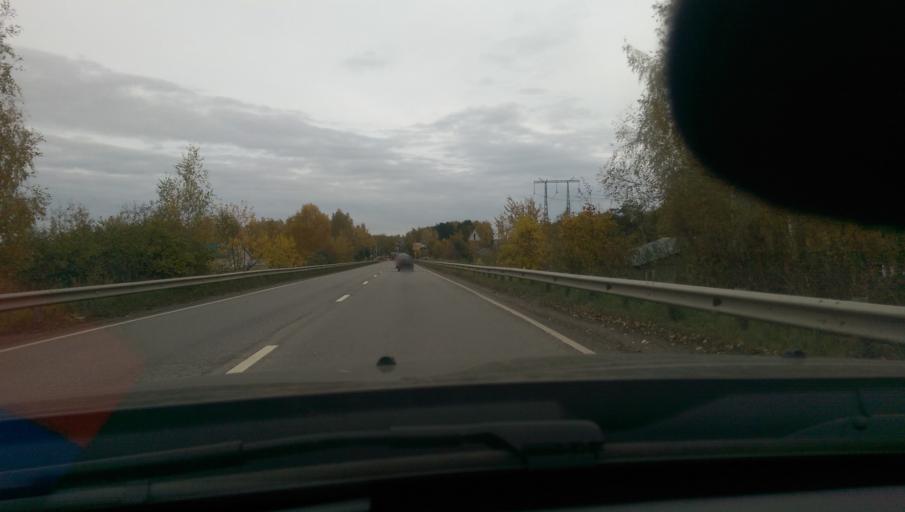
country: RU
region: Moskovskaya
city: Pirogovskiy
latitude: 55.9700
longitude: 37.7027
